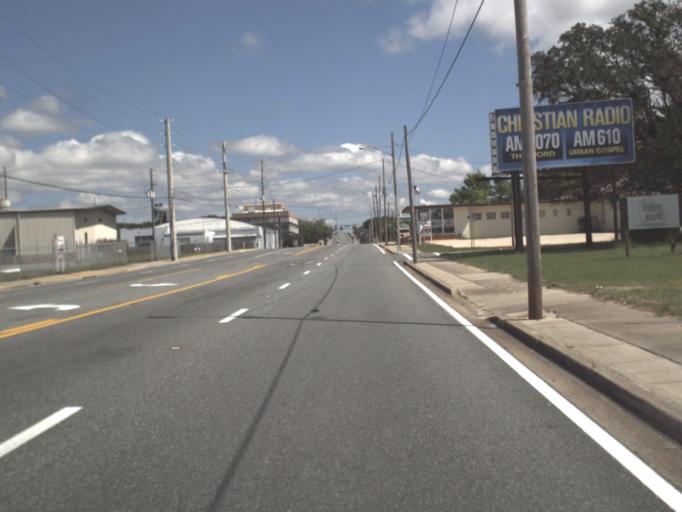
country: US
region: Florida
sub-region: Escambia County
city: Pensacola
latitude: 30.4095
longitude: -87.2418
